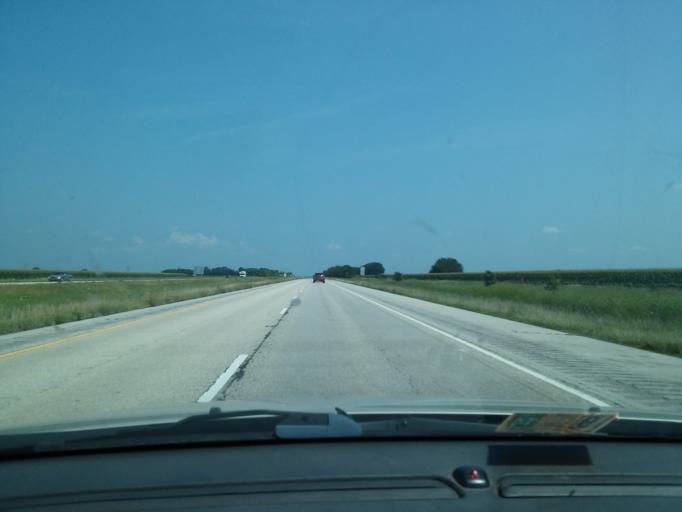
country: US
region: Illinois
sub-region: Sangamon County
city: New Berlin
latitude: 39.7368
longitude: -90.0311
